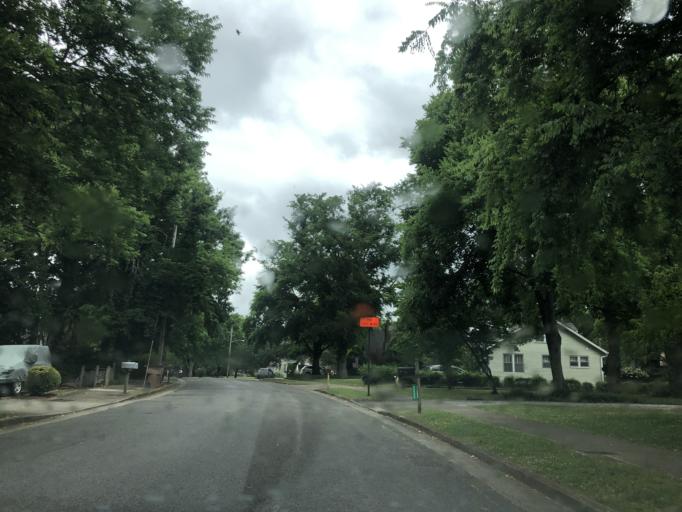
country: US
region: Tennessee
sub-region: Davidson County
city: Nashville
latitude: 36.1289
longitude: -86.8152
